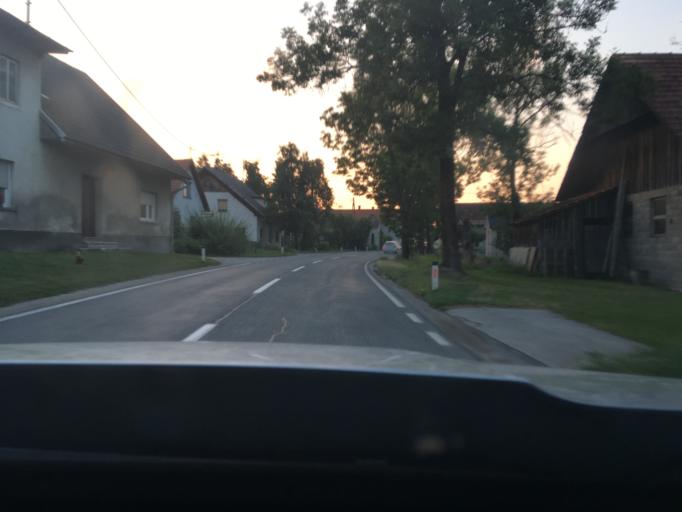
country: SI
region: Ribnica
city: Ribnica
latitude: 45.7216
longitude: 14.7429
